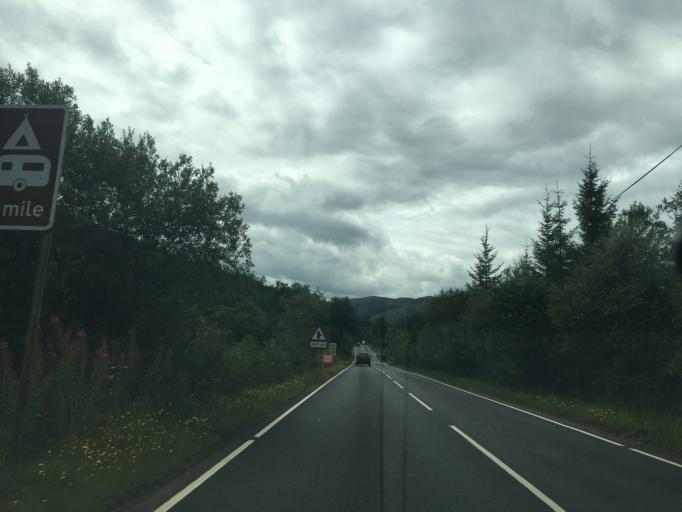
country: GB
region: Scotland
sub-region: Stirling
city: Callander
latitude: 56.3650
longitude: -4.3014
